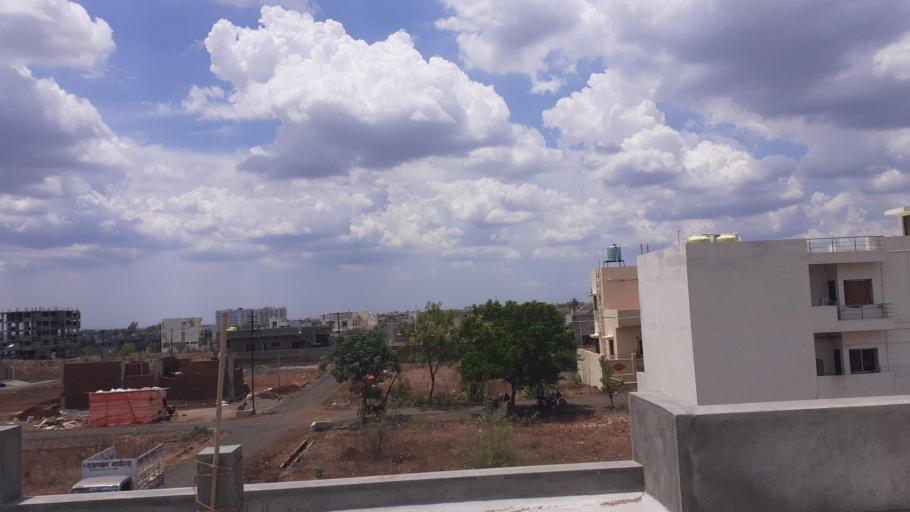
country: IN
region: Maharashtra
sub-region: Amravati Division
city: Amravati
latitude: 20.9556
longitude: 77.7915
